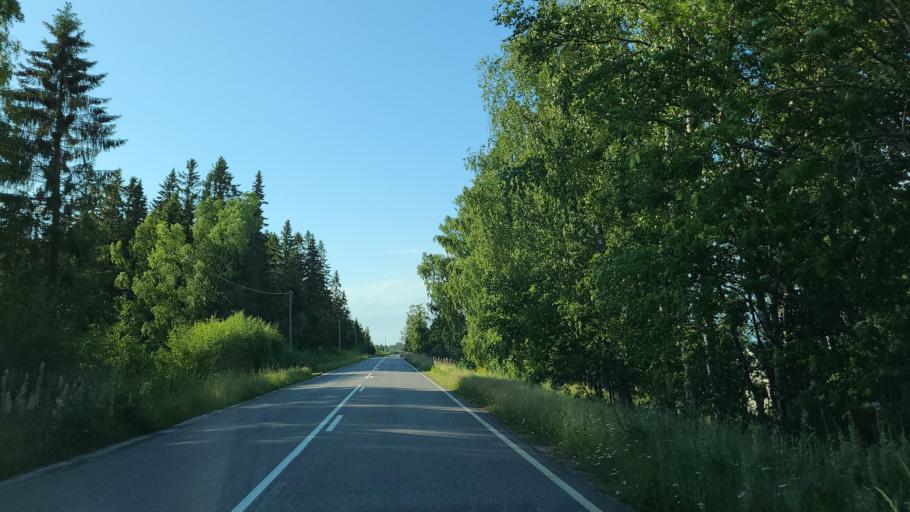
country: FI
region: Ostrobothnia
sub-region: Vaasa
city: Replot
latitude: 63.2684
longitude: 21.3475
